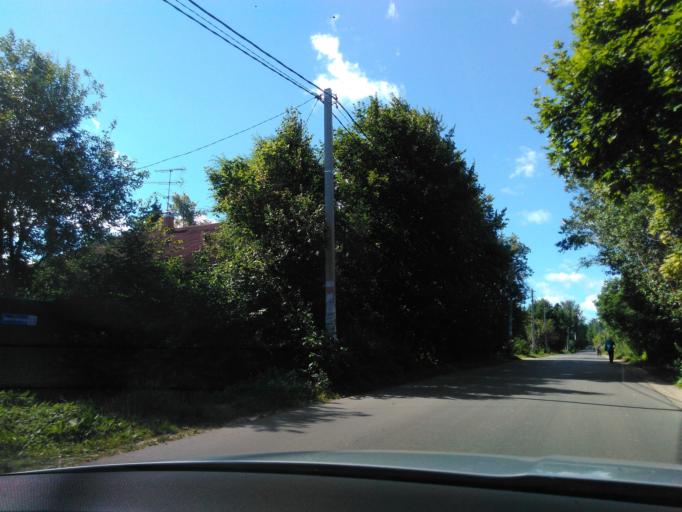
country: RU
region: Moskovskaya
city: Klin
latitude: 56.2346
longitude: 36.8236
